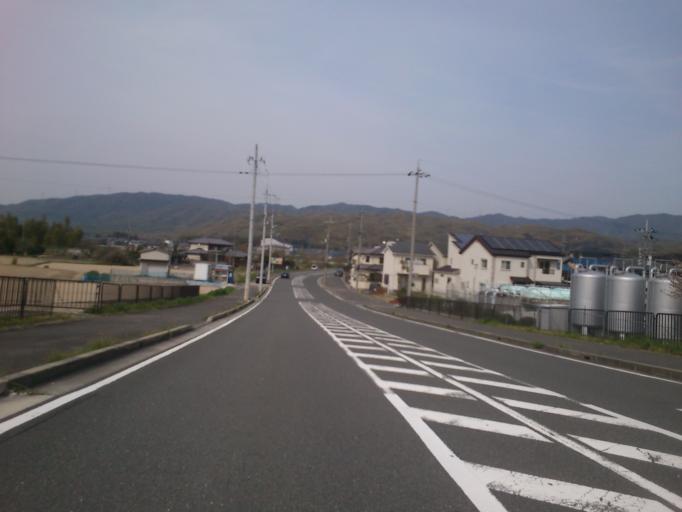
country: JP
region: Kyoto
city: Tanabe
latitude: 34.7706
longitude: 135.8073
